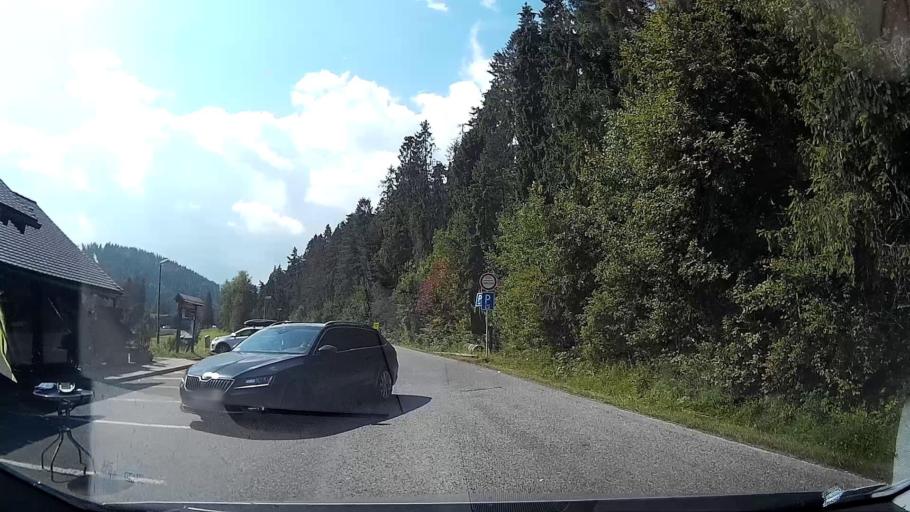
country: SK
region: Kosicky
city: Spisska Nova Ves
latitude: 48.9465
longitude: 20.4847
